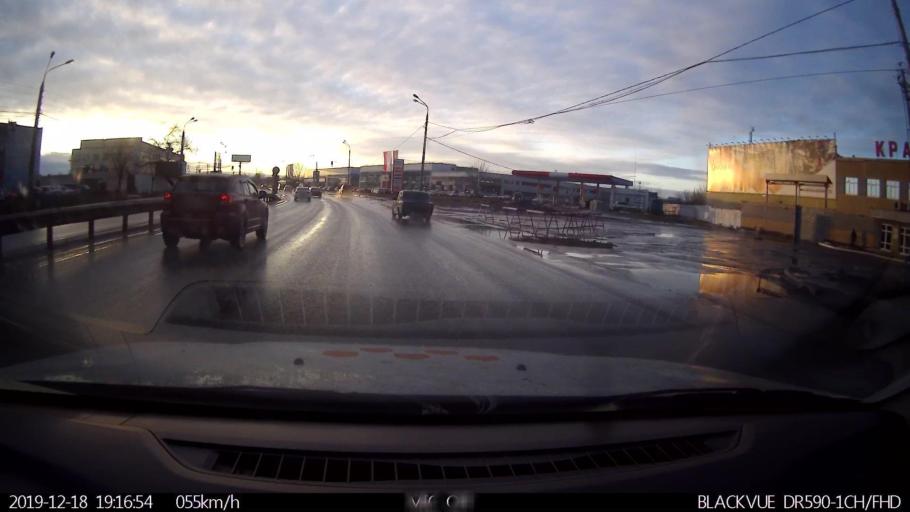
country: RU
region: Nizjnij Novgorod
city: Nizhniy Novgorod
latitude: 56.3111
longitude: 43.8994
